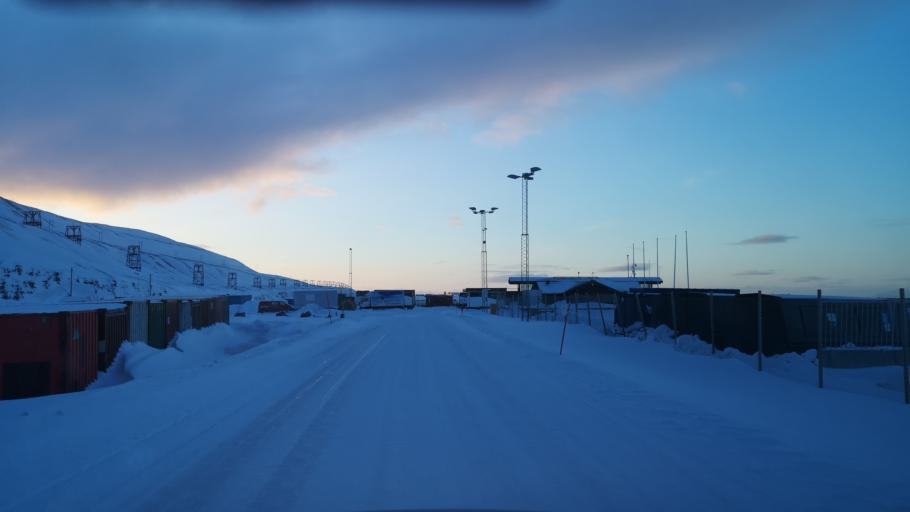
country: SJ
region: Svalbard
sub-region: Spitsbergen
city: Longyearbyen
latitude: 78.2281
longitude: 15.6006
